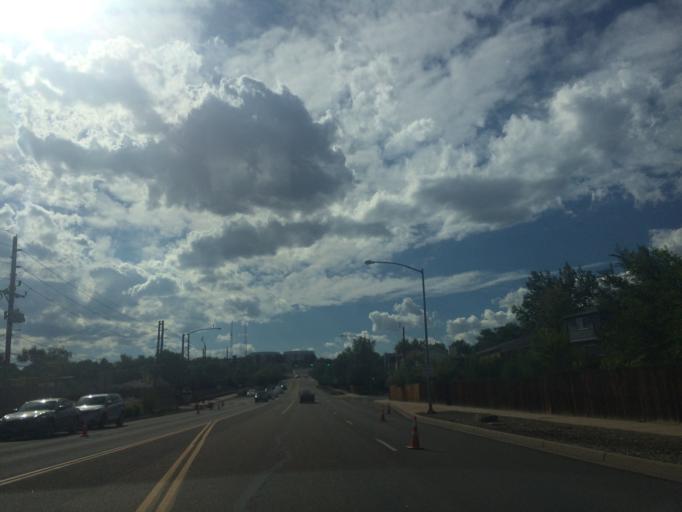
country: US
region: Colorado
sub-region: Adams County
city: Thornton
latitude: 39.8707
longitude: -104.9656
